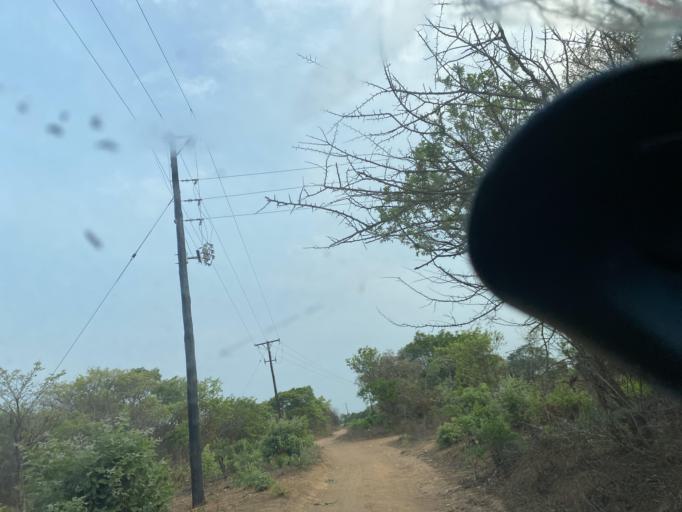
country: ZM
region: Lusaka
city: Chongwe
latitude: -15.2055
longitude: 28.4987
